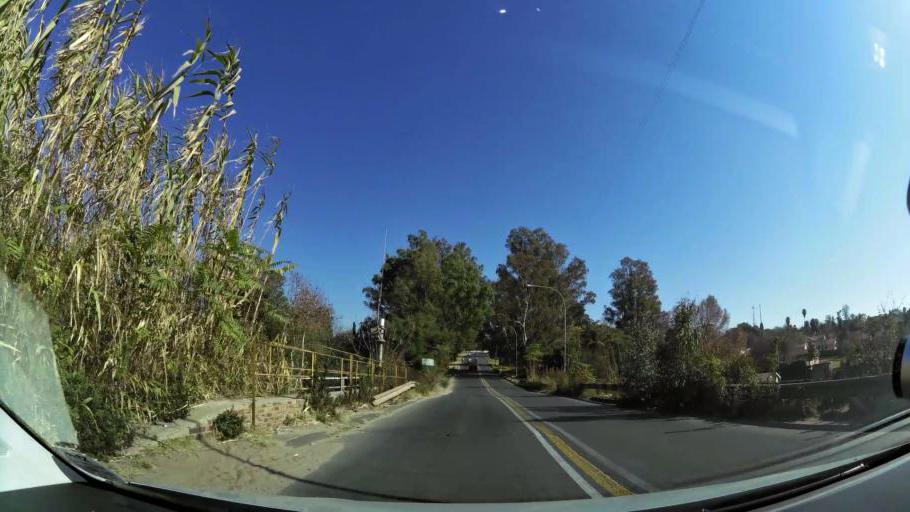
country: ZA
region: Gauteng
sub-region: City of Johannesburg Metropolitan Municipality
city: Modderfontein
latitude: -26.1190
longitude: 28.1122
